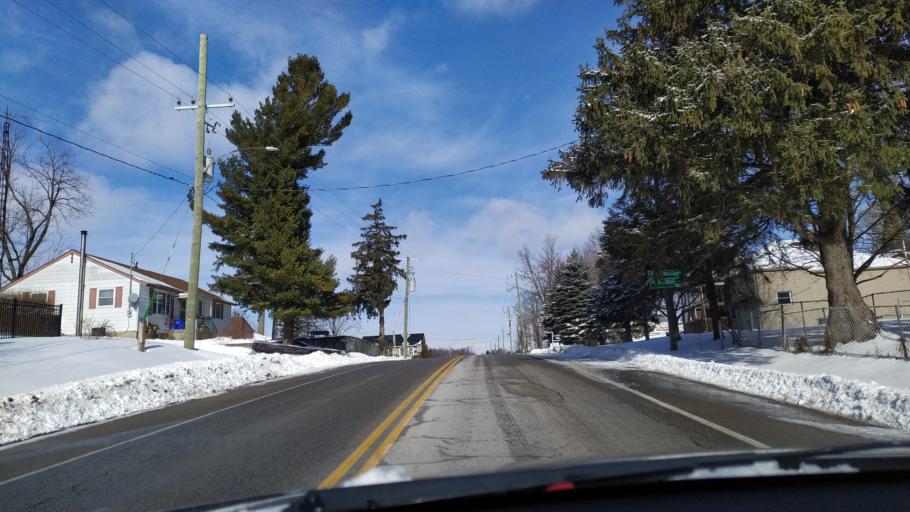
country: CA
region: Ontario
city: Waterloo
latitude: 43.4880
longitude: -80.6886
